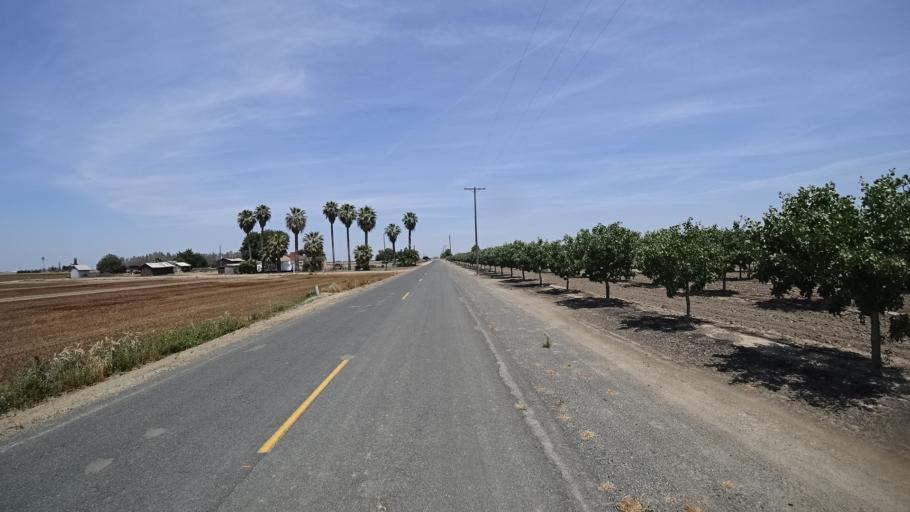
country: US
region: California
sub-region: Fresno County
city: Riverdale
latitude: 36.3989
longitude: -119.8342
